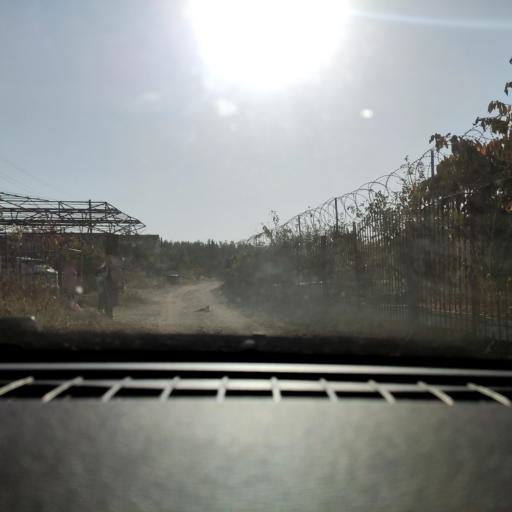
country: RU
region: Voronezj
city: Maslovka
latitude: 51.6070
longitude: 39.2163
